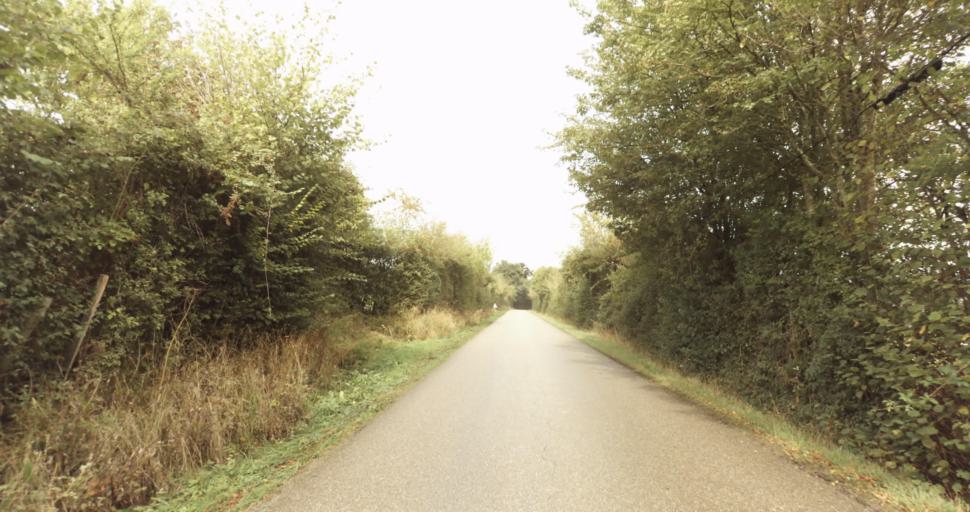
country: FR
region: Lower Normandy
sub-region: Departement de l'Orne
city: Vimoutiers
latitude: 48.8507
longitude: 0.2097
